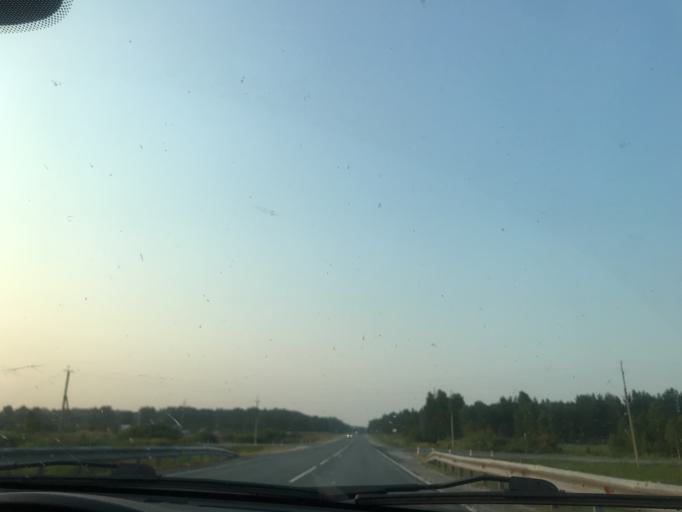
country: RU
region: Novosibirsk
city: Dorogino
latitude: 54.3742
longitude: 83.3048
